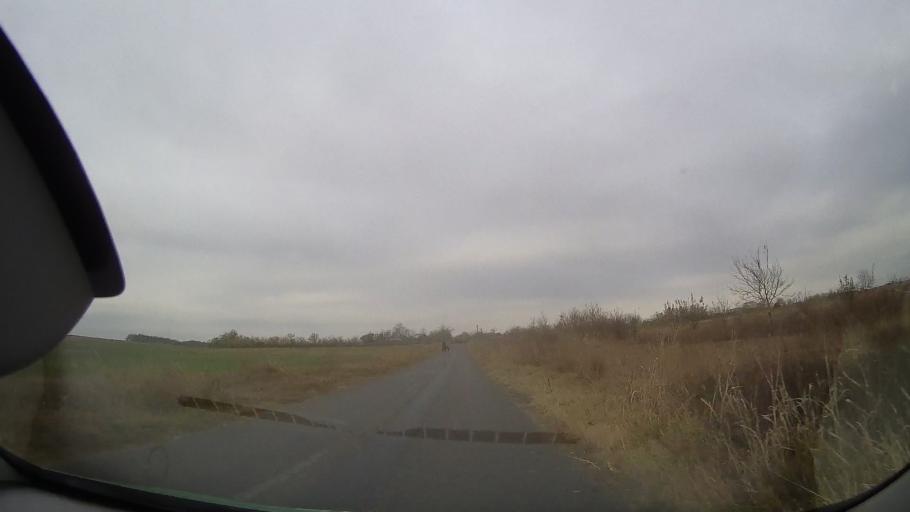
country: RO
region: Buzau
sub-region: Comuna Largu
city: Largu
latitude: 44.9694
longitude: 27.1844
